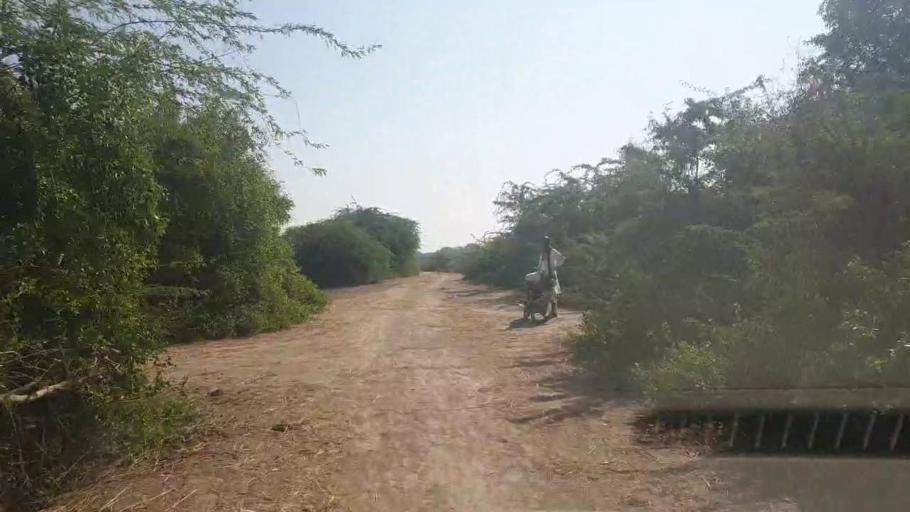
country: PK
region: Sindh
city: Badin
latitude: 24.7149
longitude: 68.8908
